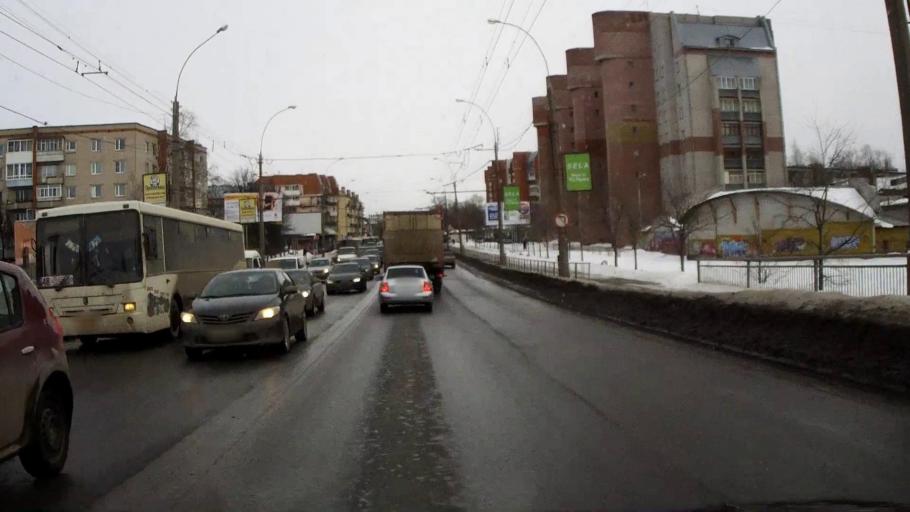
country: RU
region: Vologda
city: Vologda
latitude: 59.2181
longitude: 39.8651
